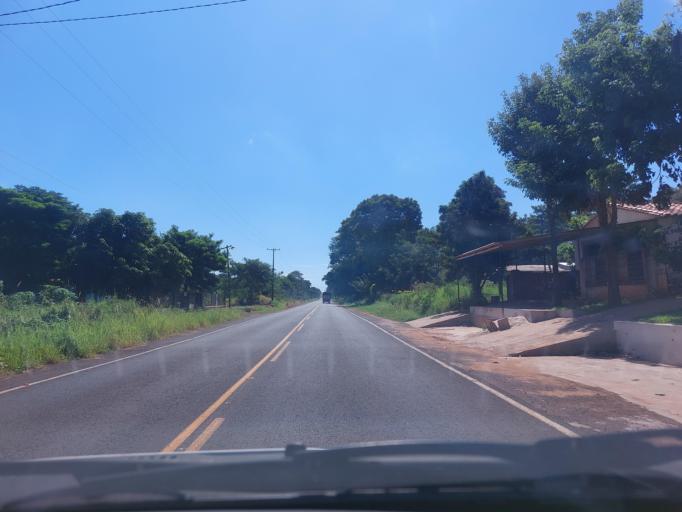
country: PY
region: San Pedro
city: Guayaybi
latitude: -24.5907
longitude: -56.5196
